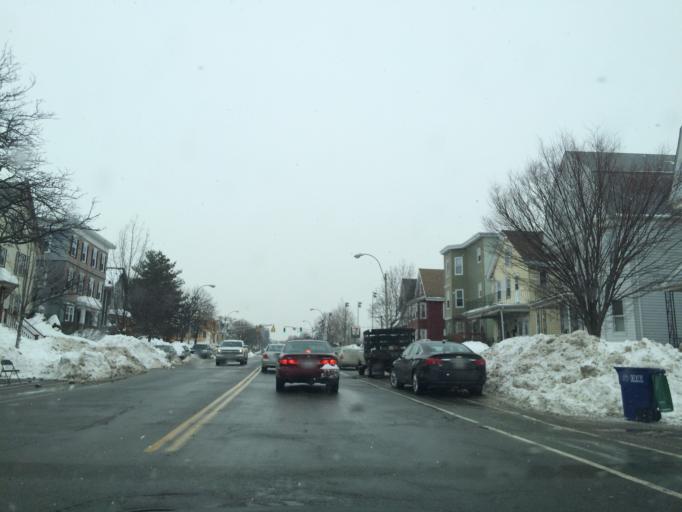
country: US
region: Massachusetts
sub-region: Middlesex County
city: Somerville
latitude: 42.3990
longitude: -71.1093
